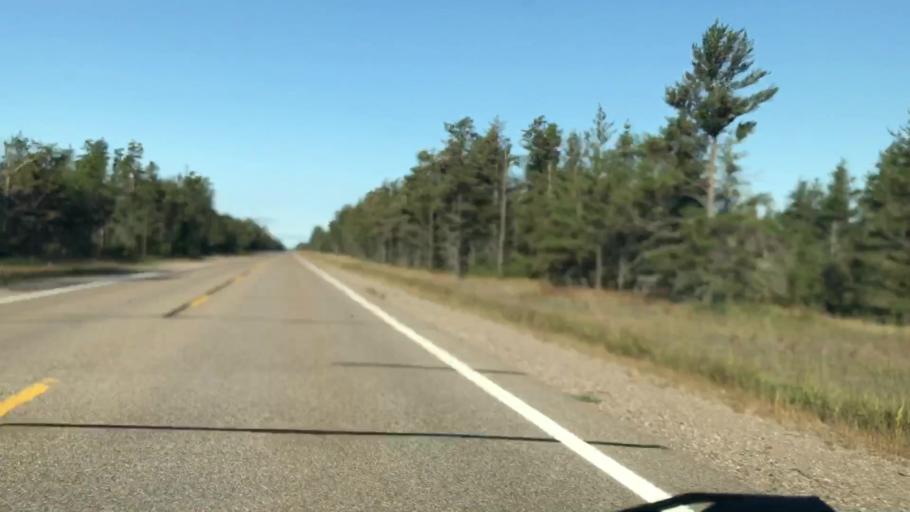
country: US
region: Michigan
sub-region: Mackinac County
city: Saint Ignace
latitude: 46.3586
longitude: -84.8346
